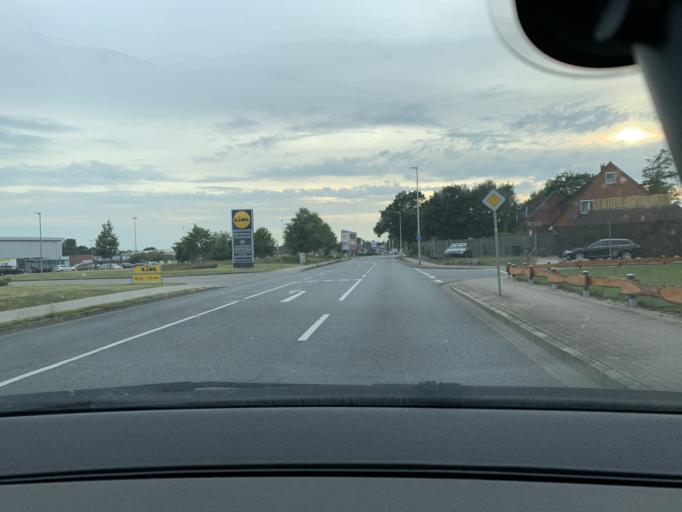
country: DE
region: Schleswig-Holstein
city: Mildstedt
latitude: 54.4709
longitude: 9.0932
